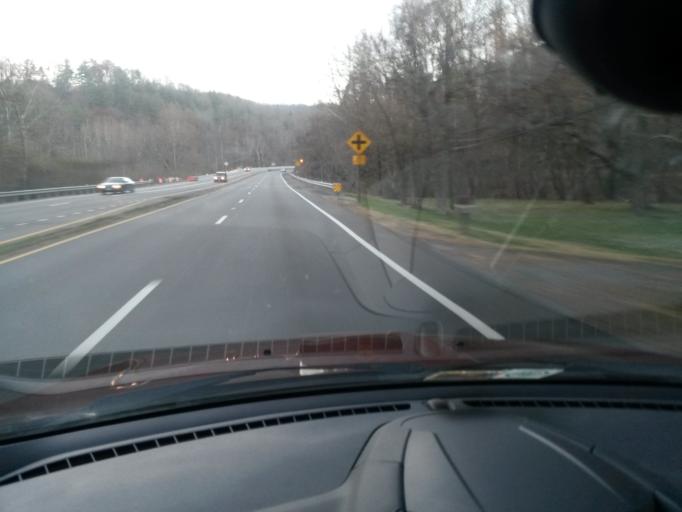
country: US
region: Virginia
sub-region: Roanoke County
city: Narrows
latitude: 37.1829
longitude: -79.9358
